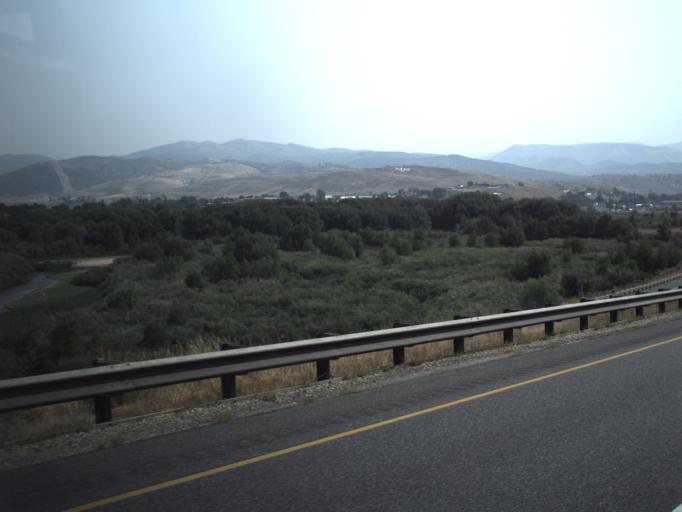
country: US
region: Utah
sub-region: Summit County
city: Coalville
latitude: 40.9219
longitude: -111.4106
